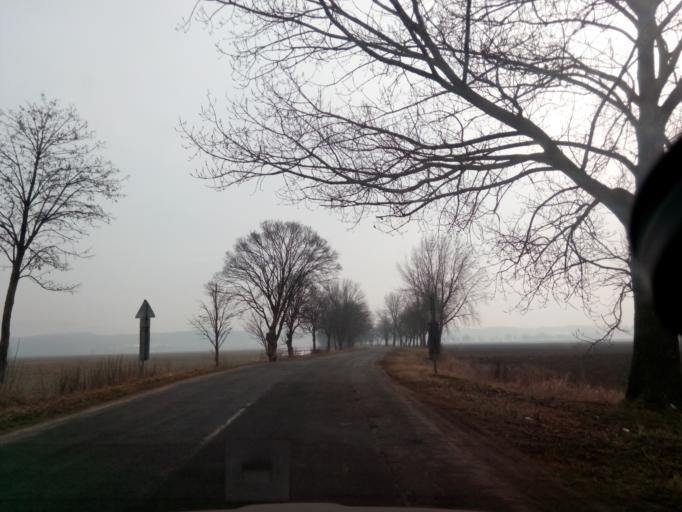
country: HU
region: Borsod-Abauj-Zemplen
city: Gonc
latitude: 48.4946
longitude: 21.2418
